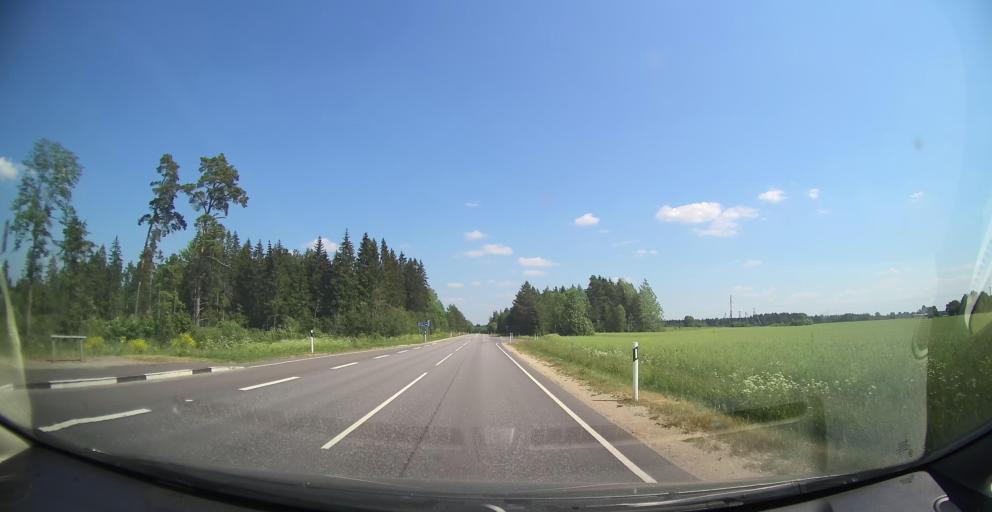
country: EE
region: Harju
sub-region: Anija vald
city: Kehra
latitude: 59.2219
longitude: 25.2479
